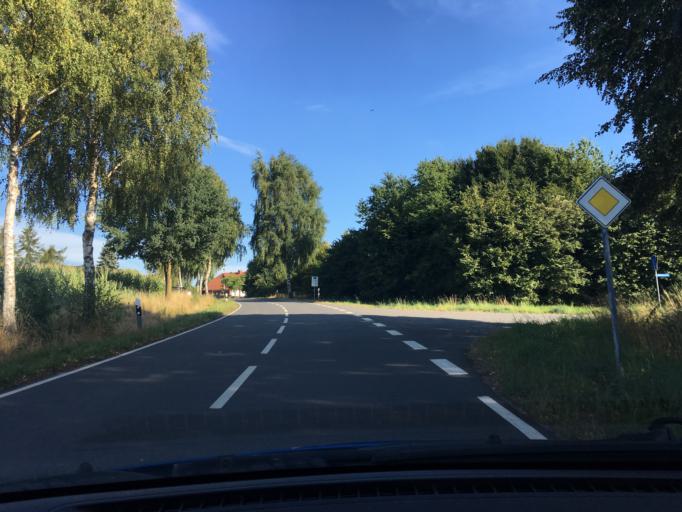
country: DE
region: Lower Saxony
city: Dahlenburg
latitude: 53.1925
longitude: 10.7210
